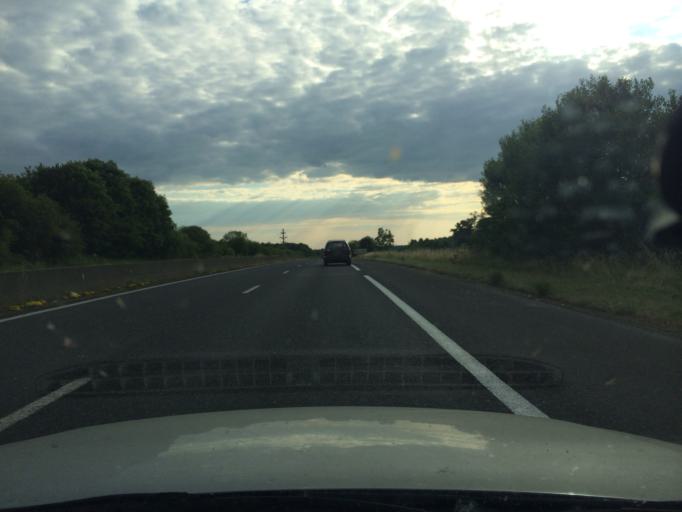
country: FR
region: Lorraine
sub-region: Departement de la Meuse
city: Ancerville
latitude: 48.6399
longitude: 5.0414
